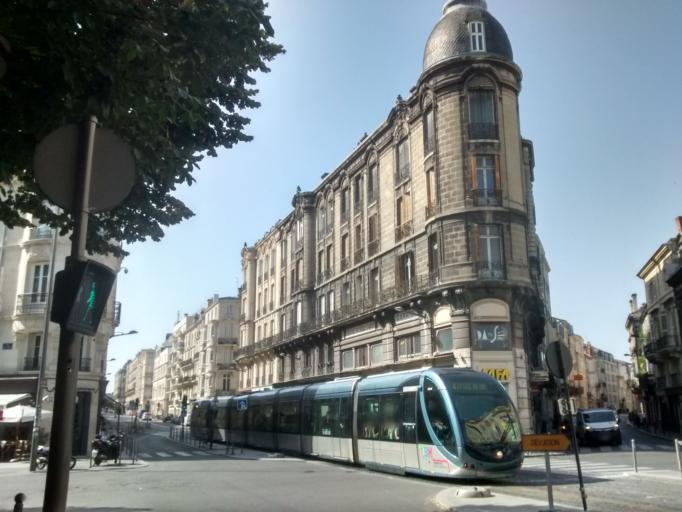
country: FR
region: Aquitaine
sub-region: Departement de la Gironde
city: Bordeaux
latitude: 44.8352
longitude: -0.5753
